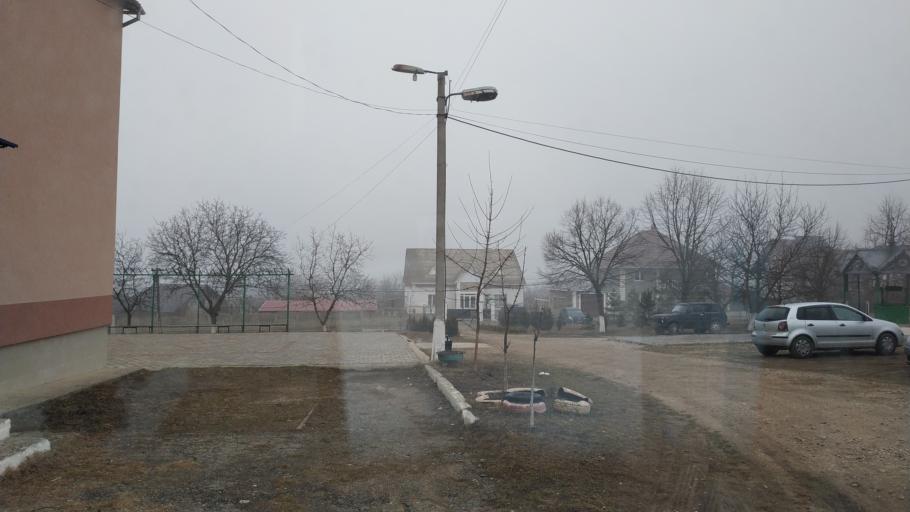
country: MD
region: Laloveni
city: Ialoveni
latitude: 46.9625
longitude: 28.7088
